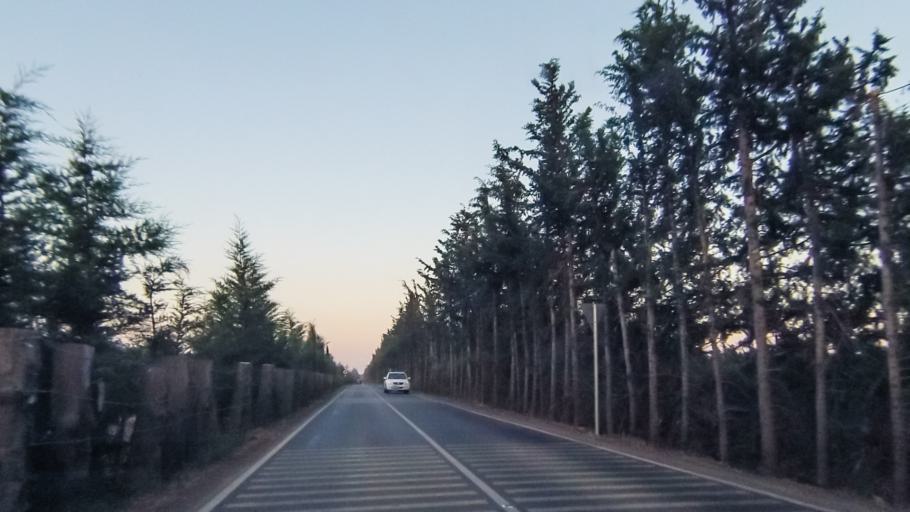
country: CY
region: Larnaka
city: Kolossi
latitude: 34.6370
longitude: 32.9476
